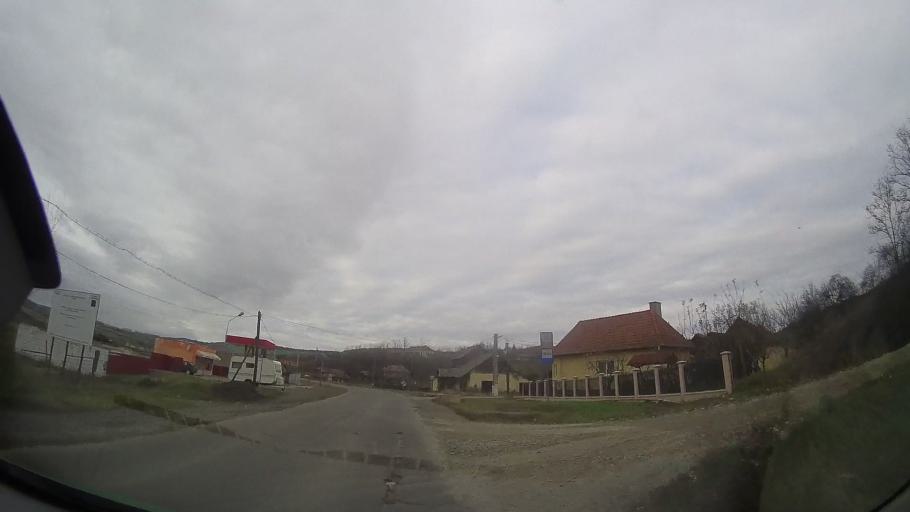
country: RO
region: Bistrita-Nasaud
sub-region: Comuna Urmenis
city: Urmenis
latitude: 46.7667
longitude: 24.3696
